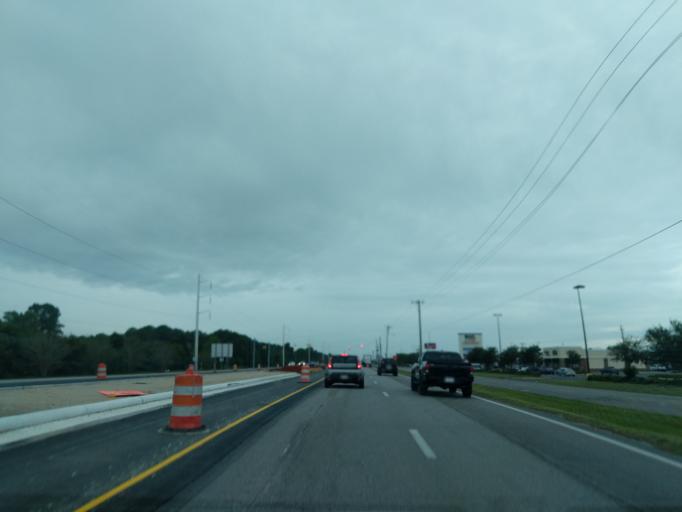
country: US
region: Mississippi
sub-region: Jackson County
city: Moss Point
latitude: 30.3840
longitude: -88.5181
